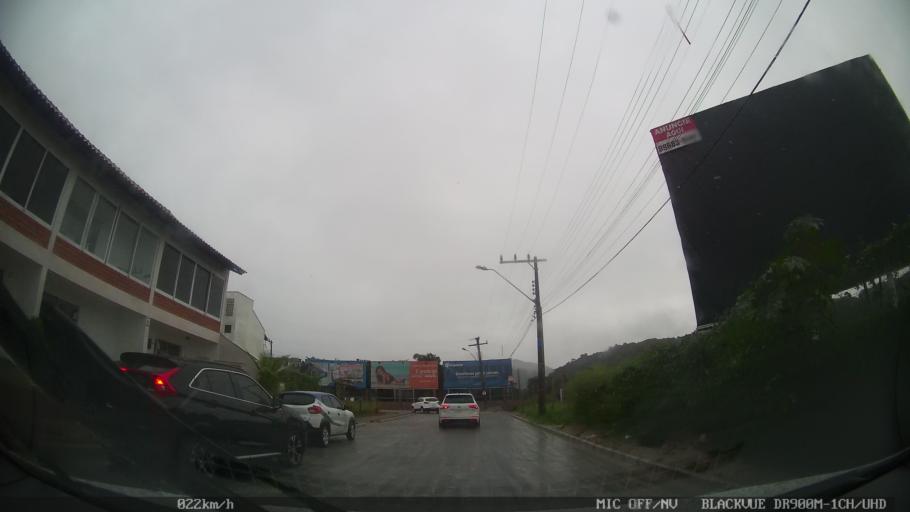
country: BR
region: Santa Catarina
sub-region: Itajai
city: Itajai
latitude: -26.9412
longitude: -48.6295
